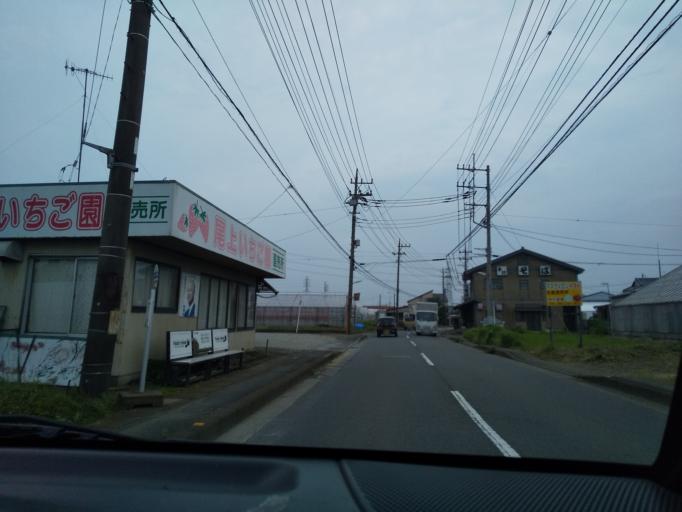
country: JP
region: Kanagawa
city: Atsugi
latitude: 35.4189
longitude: 139.3919
